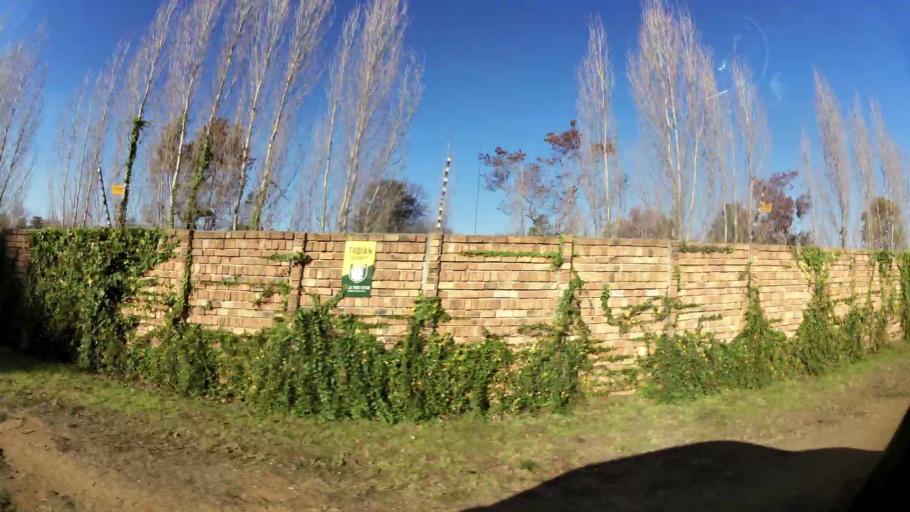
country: ZA
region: Gauteng
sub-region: City of Johannesburg Metropolitan Municipality
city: Roodepoort
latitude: -26.0933
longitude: 27.9459
